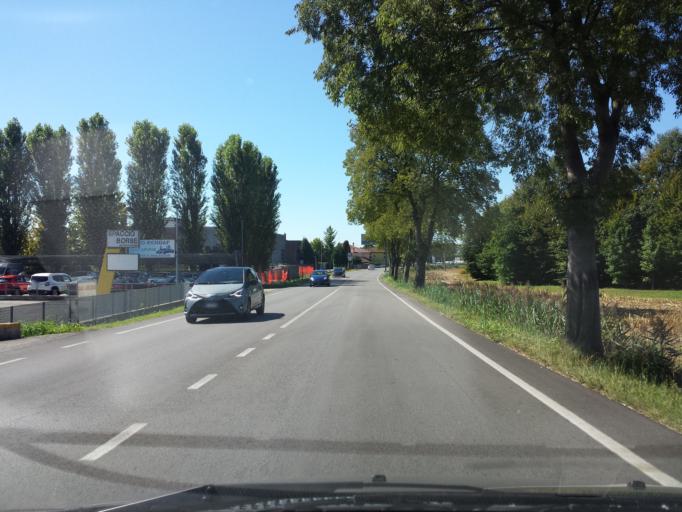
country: IT
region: Veneto
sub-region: Provincia di Vicenza
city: Monticello Conte Otto
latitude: 45.6143
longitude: 11.5652
